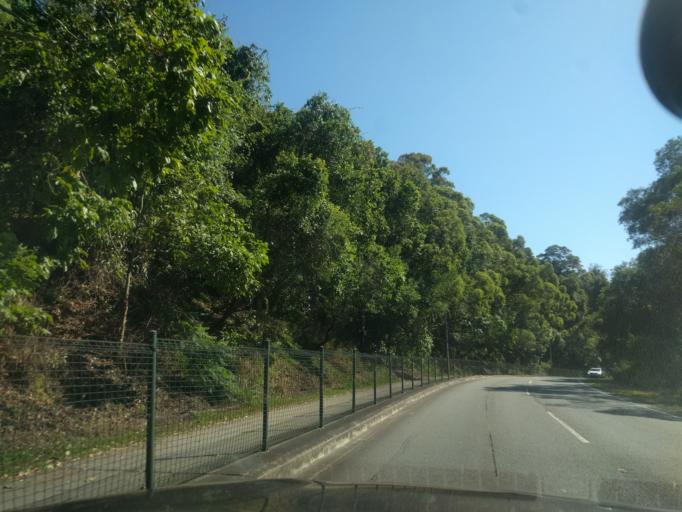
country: AU
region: Queensland
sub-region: Brisbane
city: Stafford
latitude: -27.4141
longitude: 153.0026
